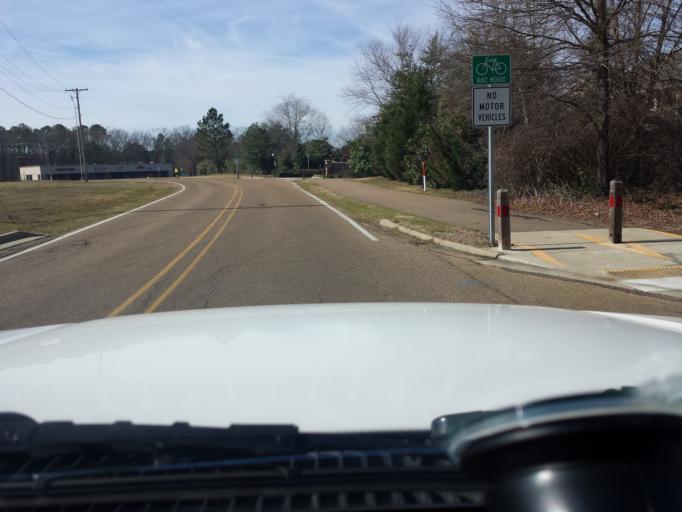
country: US
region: Mississippi
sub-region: Madison County
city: Ridgeland
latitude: 32.3848
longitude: -90.0420
